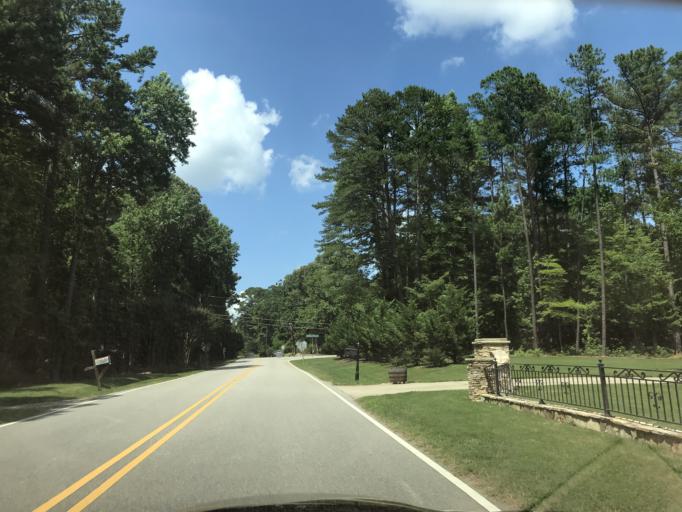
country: US
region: North Carolina
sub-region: Wake County
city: Cary
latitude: 35.8731
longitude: -78.7452
